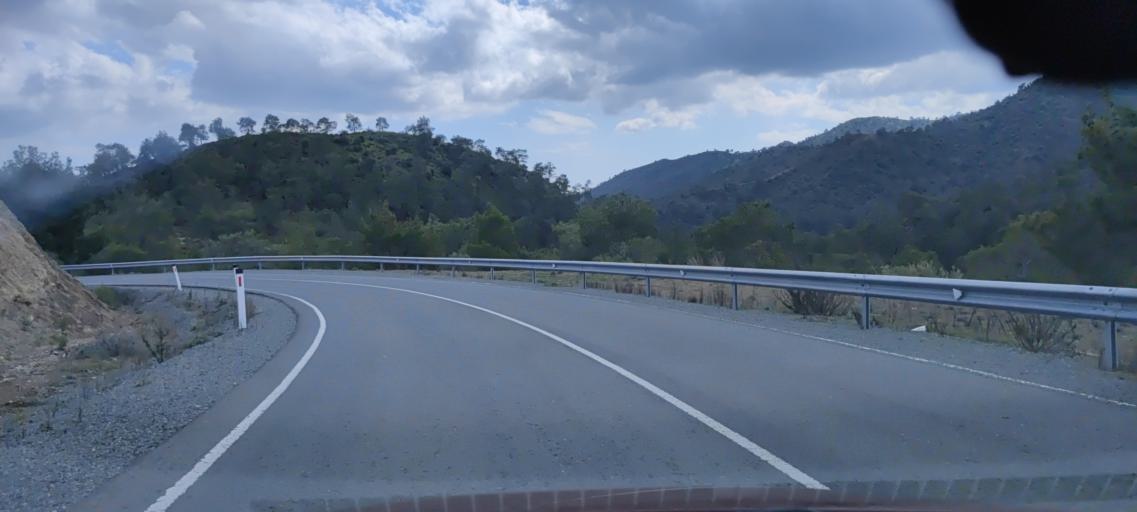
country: CY
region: Lefkosia
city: Lythrodontas
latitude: 34.9336
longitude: 33.3279
